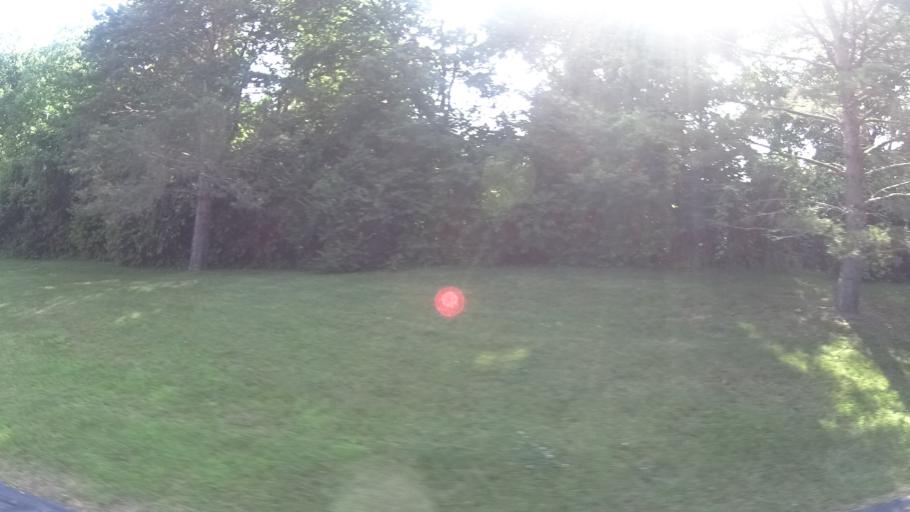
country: US
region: Ohio
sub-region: Lorain County
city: Vermilion
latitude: 41.3919
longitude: -82.4358
